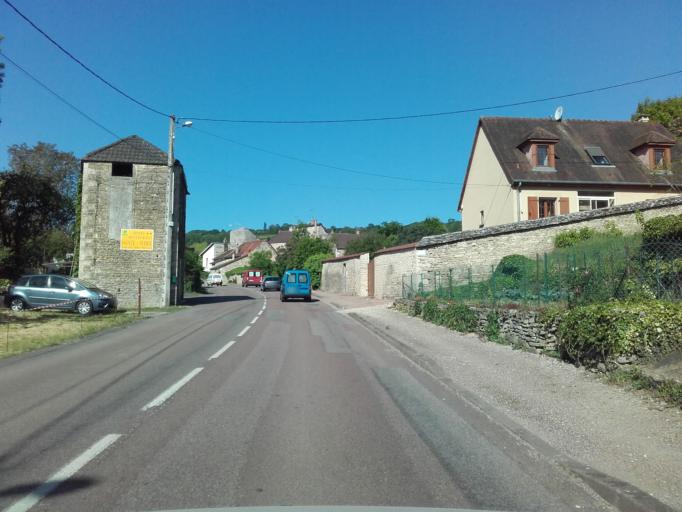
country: FR
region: Bourgogne
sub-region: Departement de la Cote-d'Or
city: Nolay
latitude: 46.9573
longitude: 4.6791
